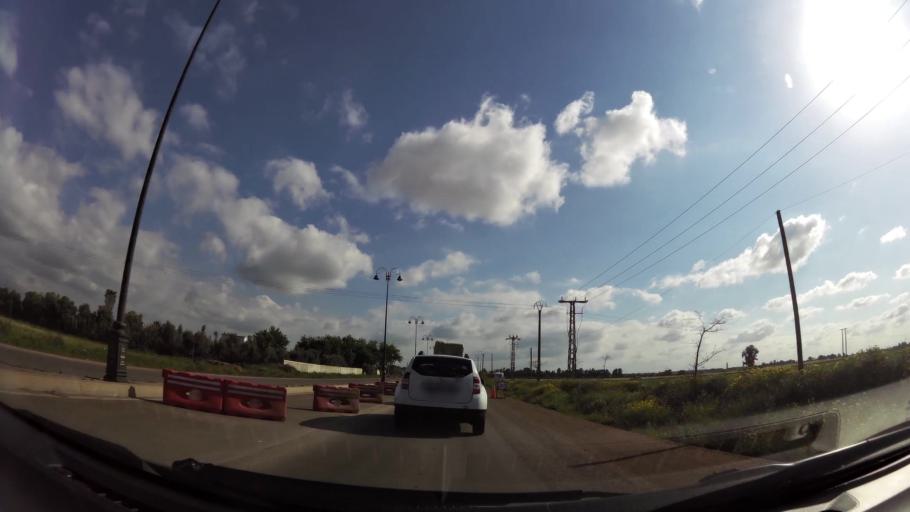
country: MA
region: Chaouia-Ouardigha
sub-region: Settat Province
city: Berrechid
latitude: 33.2920
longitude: -7.5756
